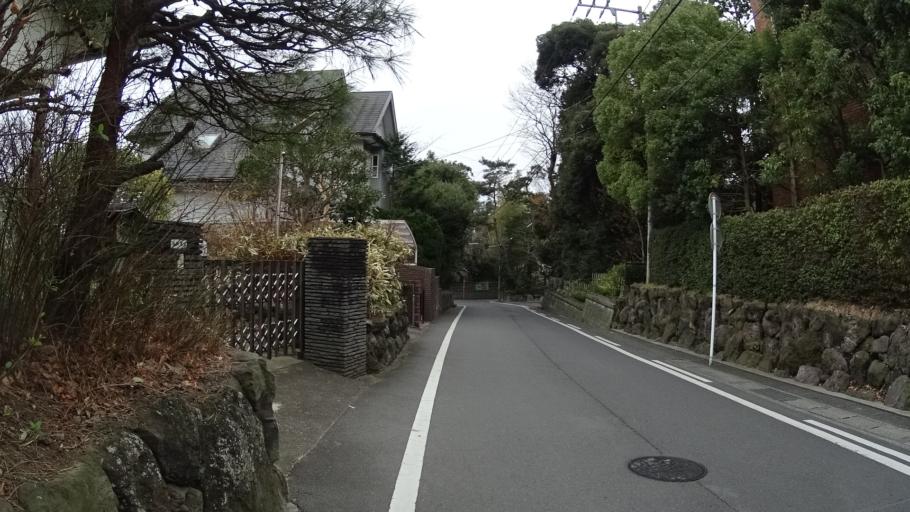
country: JP
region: Kanagawa
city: Oiso
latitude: 35.3115
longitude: 139.3077
